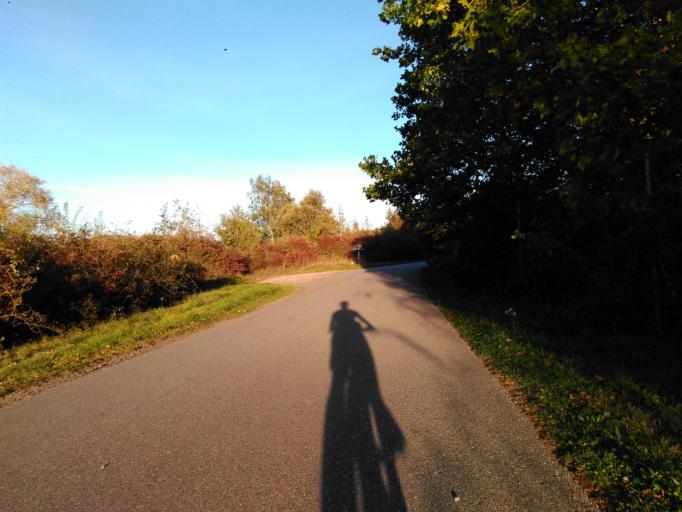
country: FR
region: Lorraine
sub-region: Departement de la Moselle
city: Argancy
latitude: 49.1950
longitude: 6.1875
